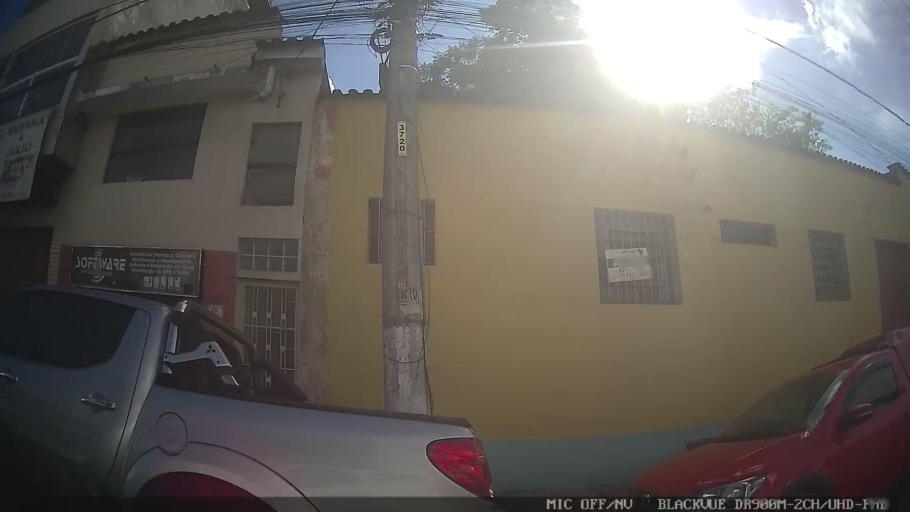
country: BR
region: Sao Paulo
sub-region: Bom Jesus Dos Perdoes
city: Bom Jesus dos Perdoes
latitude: -23.1348
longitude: -46.4645
